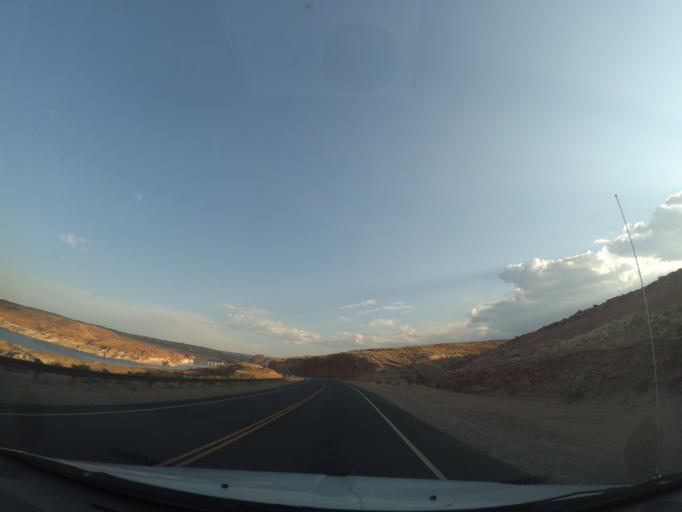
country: US
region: Arizona
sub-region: Coconino County
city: Page
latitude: 36.9590
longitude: -111.4940
